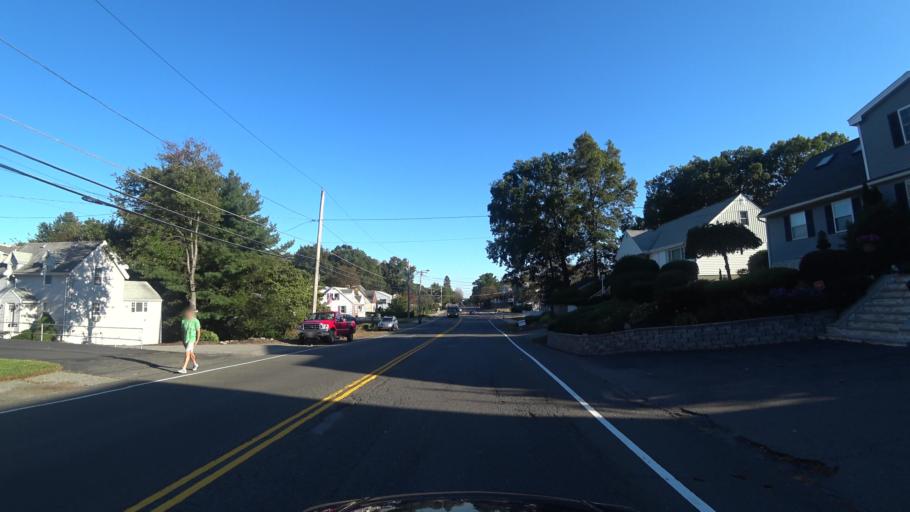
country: US
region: Massachusetts
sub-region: Middlesex County
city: Medford
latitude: 42.4397
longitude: -71.0906
